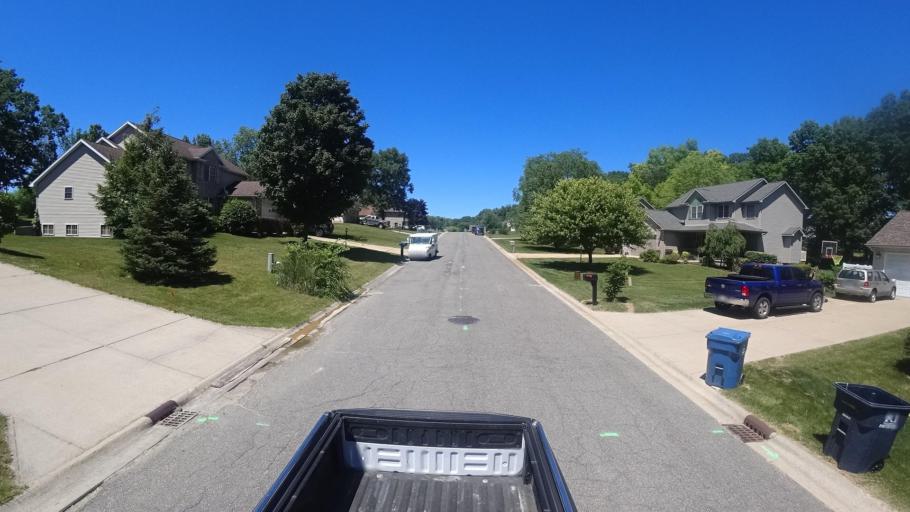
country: US
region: Indiana
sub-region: Porter County
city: Porter
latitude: 41.6314
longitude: -87.0731
